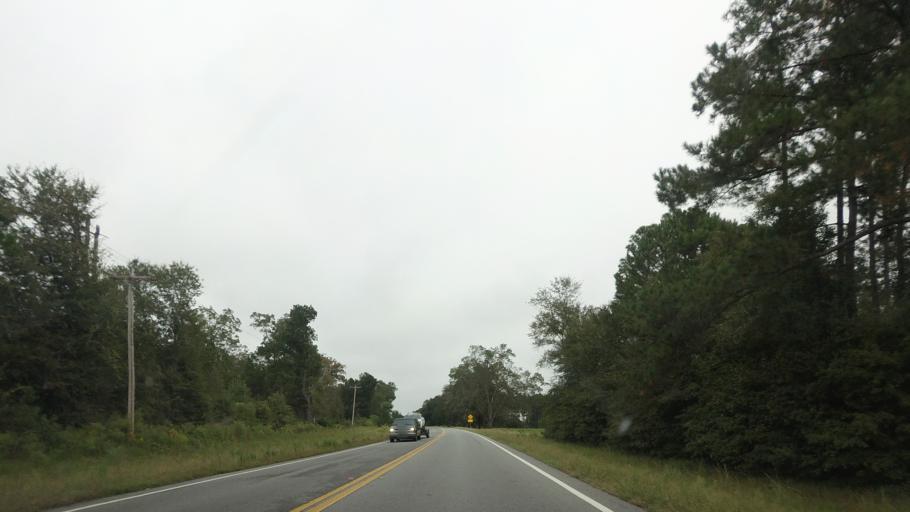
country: US
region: Georgia
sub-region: Berrien County
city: Nashville
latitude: 31.3009
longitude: -83.2336
